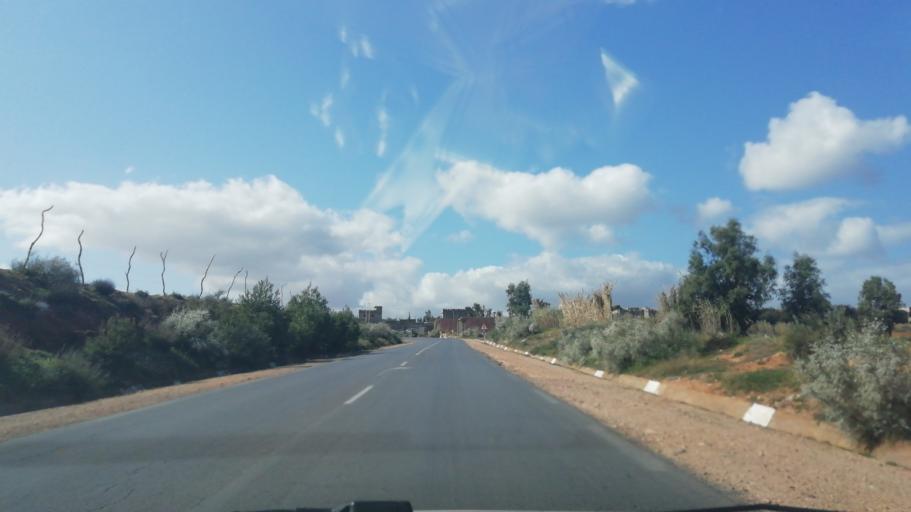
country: DZ
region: Relizane
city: Mazouna
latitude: 36.2888
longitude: 0.6486
